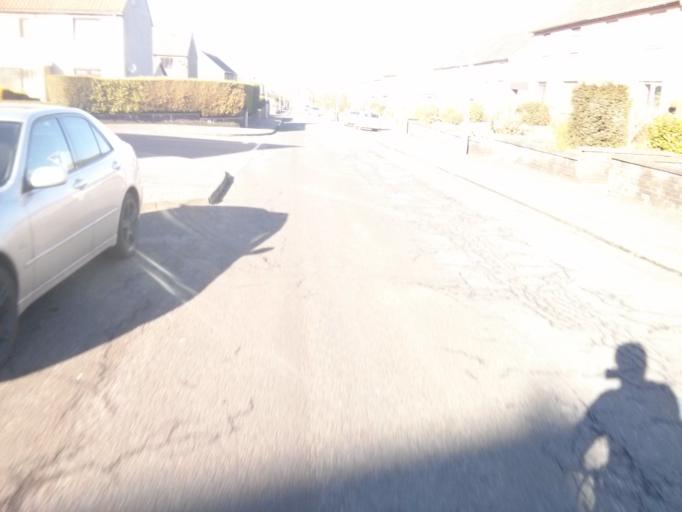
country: GB
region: Scotland
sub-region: Fife
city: Saint Andrews
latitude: 56.3288
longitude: -2.7937
